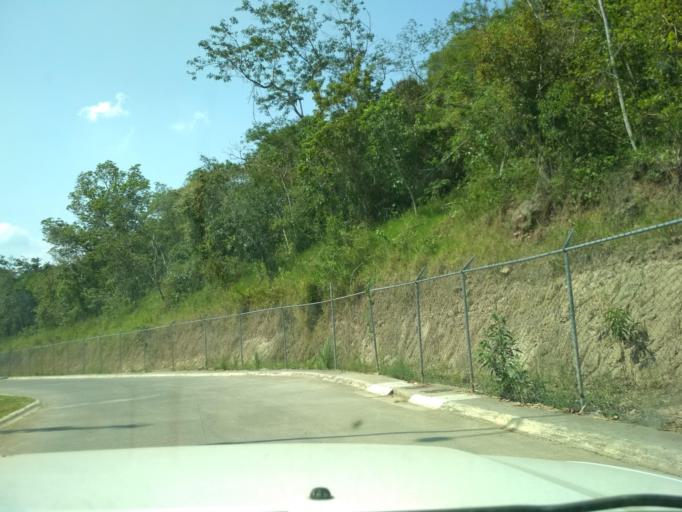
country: MX
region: Veracruz
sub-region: Emiliano Zapata
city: Las Trancas
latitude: 19.5246
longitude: -96.8637
